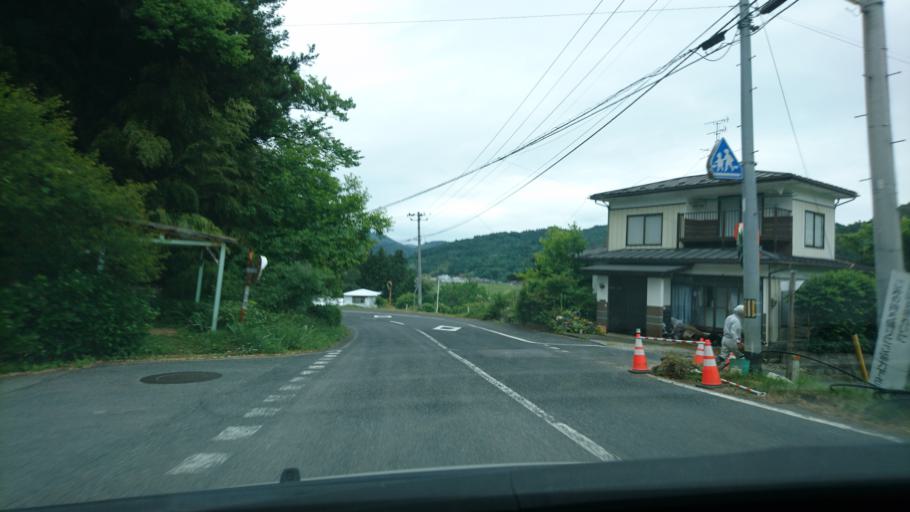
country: JP
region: Iwate
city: Ichinoseki
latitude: 38.9520
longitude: 141.2571
